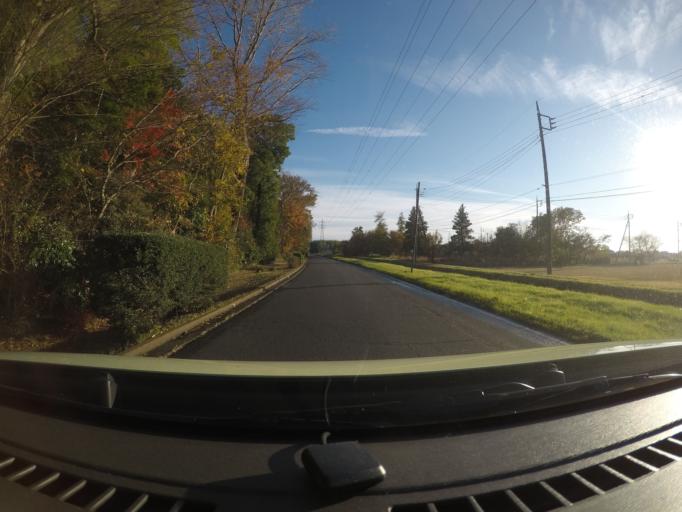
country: JP
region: Ibaraki
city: Tsukuba
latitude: 36.1168
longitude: 140.0919
